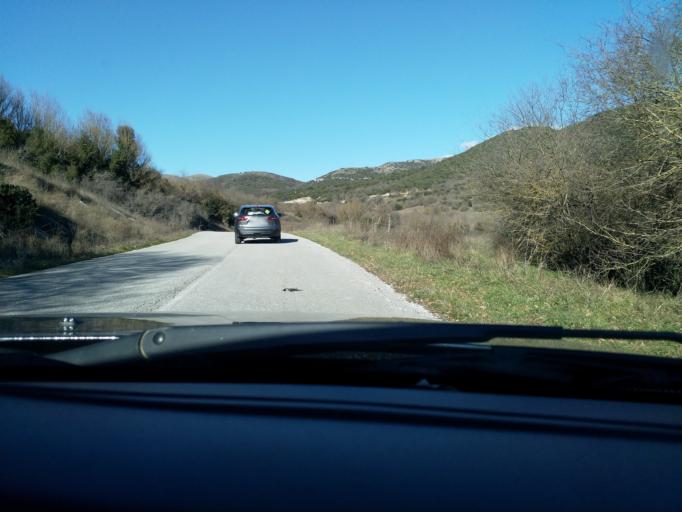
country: GR
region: Epirus
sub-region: Nomos Ioanninon
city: Kalpaki
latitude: 39.8929
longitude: 20.6717
